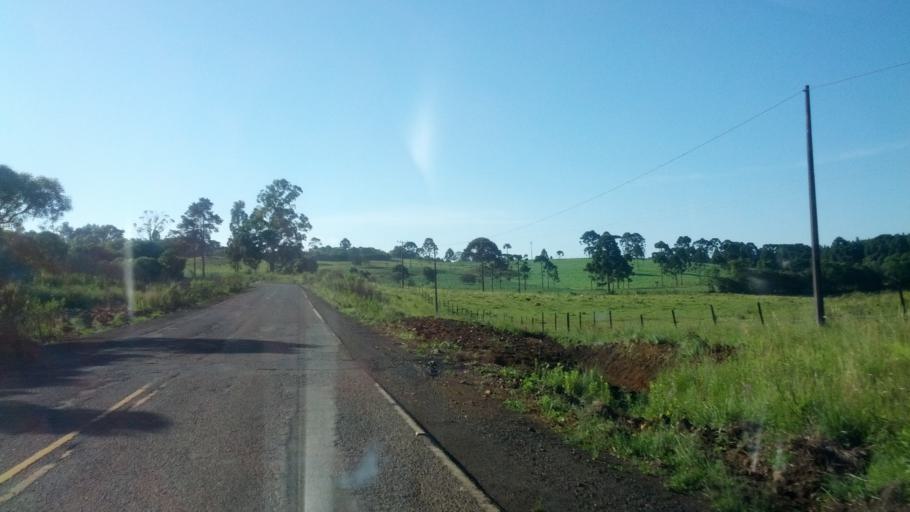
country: BR
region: Santa Catarina
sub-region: Lages
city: Lages
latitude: -27.9194
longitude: -50.5717
